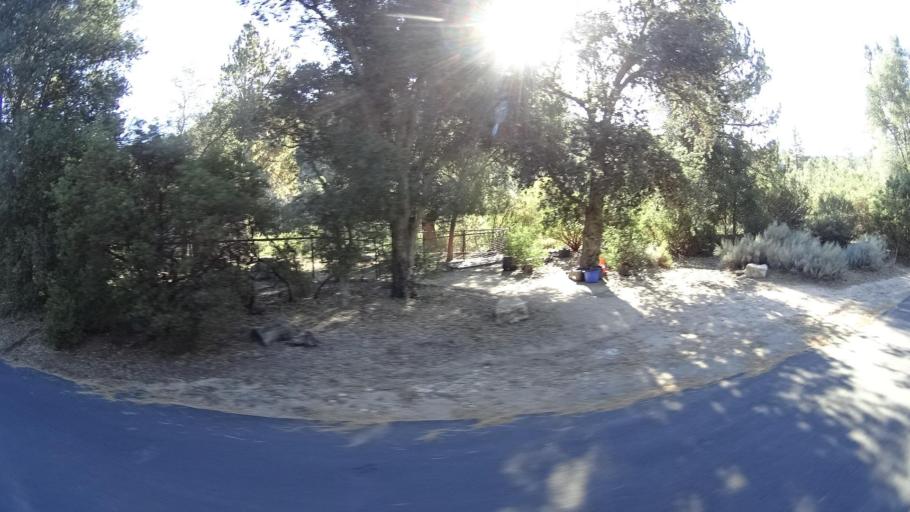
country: US
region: California
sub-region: San Diego County
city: Pine Valley
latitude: 32.8452
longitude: -116.5272
